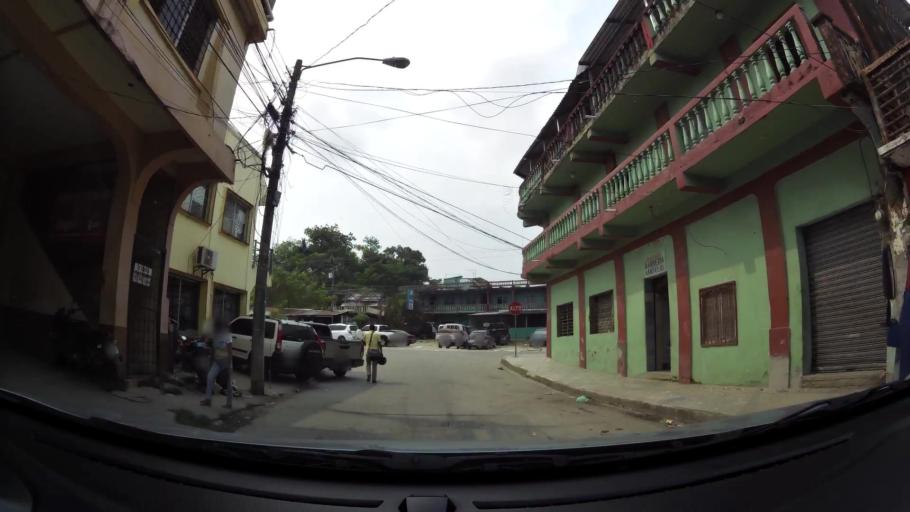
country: HN
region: Atlantida
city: Tela
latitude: 15.7812
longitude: -87.4501
